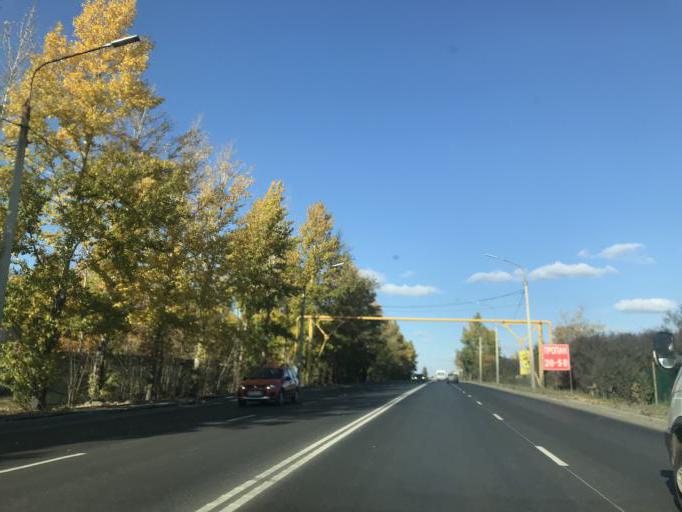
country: RU
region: Chelyabinsk
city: Roshchino
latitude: 55.2377
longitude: 61.3178
